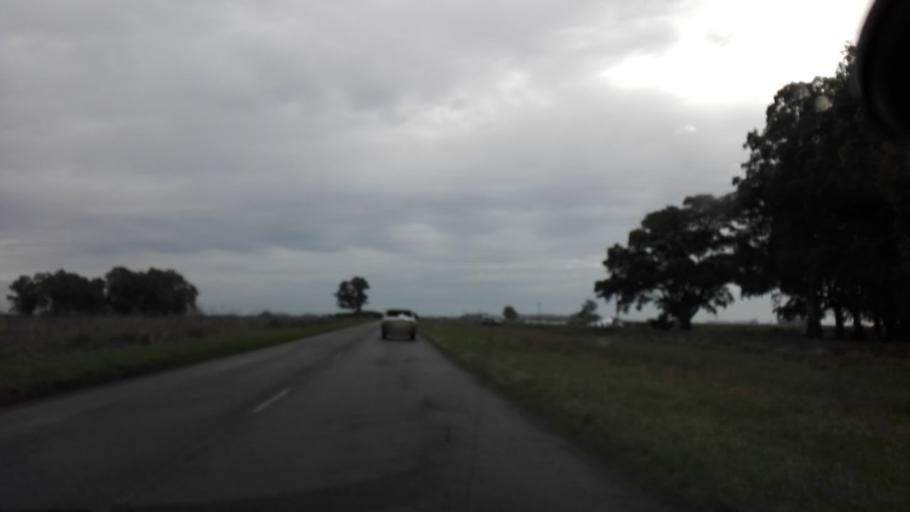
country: AR
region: Buenos Aires
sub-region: Partido de Rauch
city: Rauch
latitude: -36.6626
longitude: -59.0644
